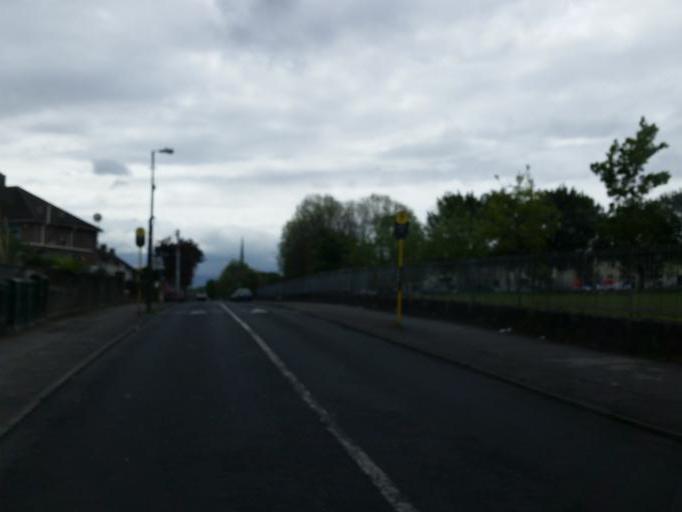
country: IE
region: Leinster
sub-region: Dublin City
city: Finglas
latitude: 53.3927
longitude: -6.3116
